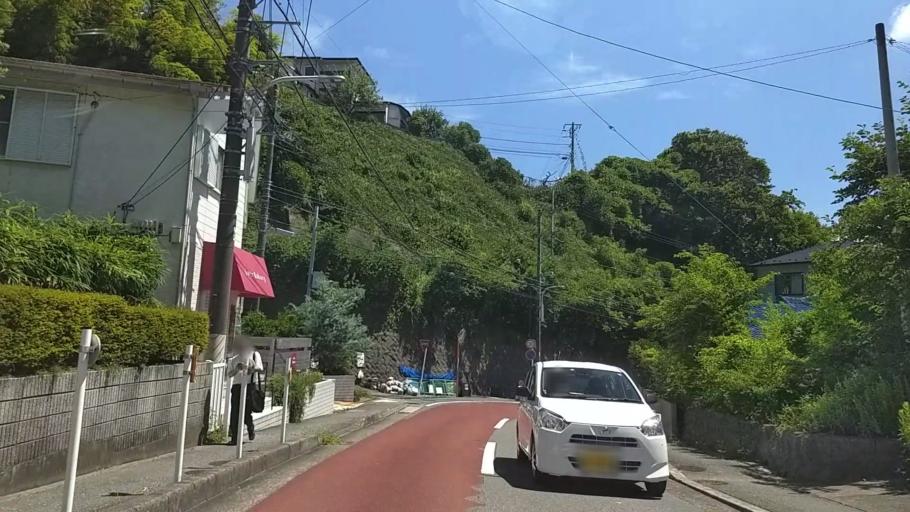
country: JP
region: Kanagawa
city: Zushi
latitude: 35.3013
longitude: 139.6009
